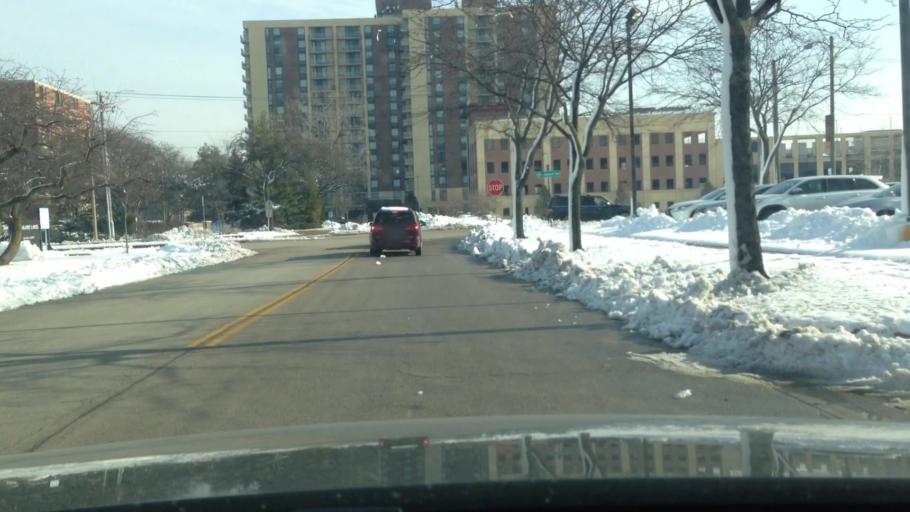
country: US
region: Illinois
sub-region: DuPage County
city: Downers Grove
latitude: 41.8437
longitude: -88.0122
